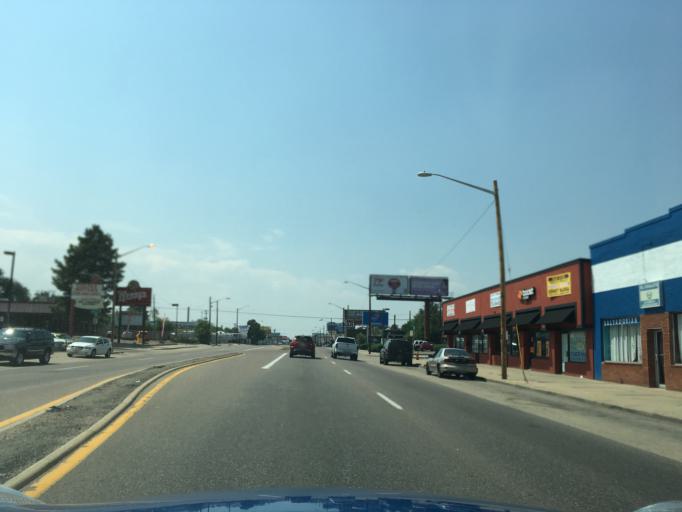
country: US
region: Colorado
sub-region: Arapahoe County
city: Glendale
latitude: 39.7402
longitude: -104.8931
